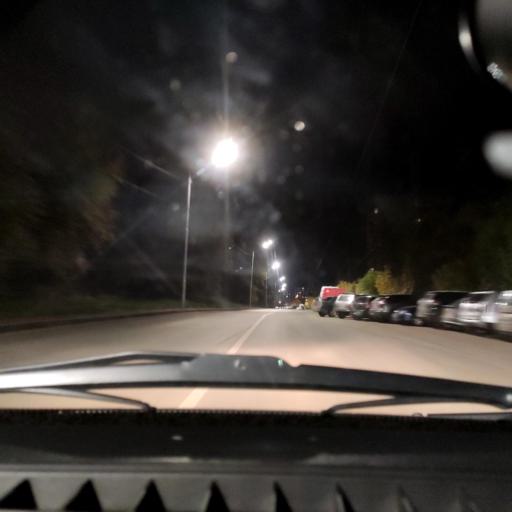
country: RU
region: Bashkortostan
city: Ufa
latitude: 54.7071
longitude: 56.0086
